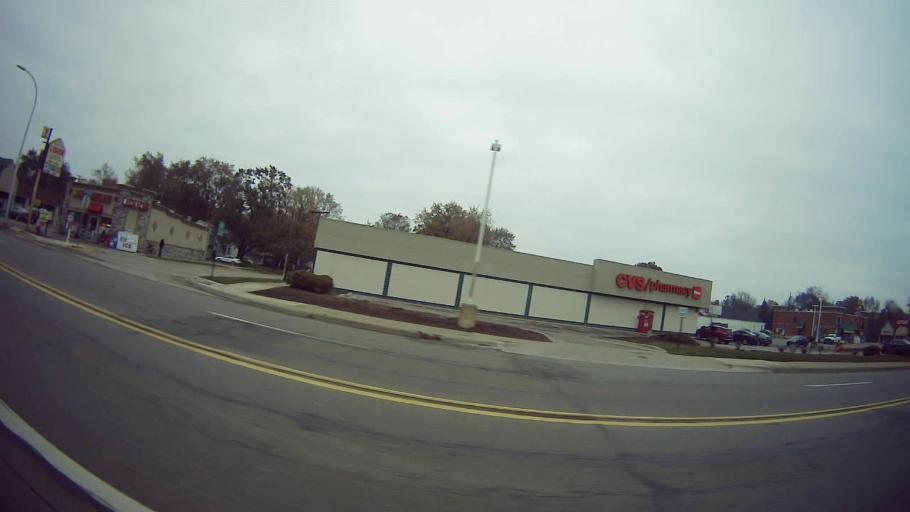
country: US
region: Michigan
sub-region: Oakland County
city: Clawson
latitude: 42.5347
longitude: -83.1356
